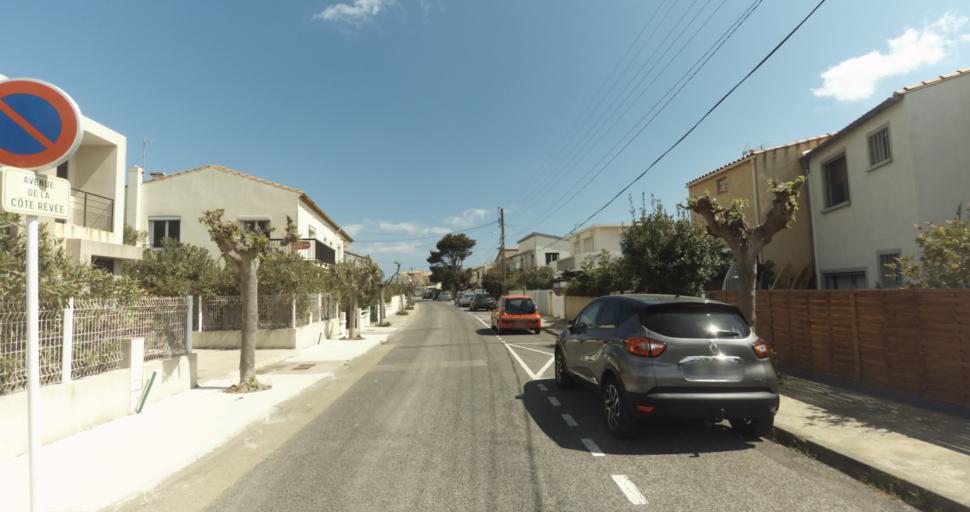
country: FR
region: Languedoc-Roussillon
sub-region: Departement de l'Aude
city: Leucate
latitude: 42.9043
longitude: 3.0532
